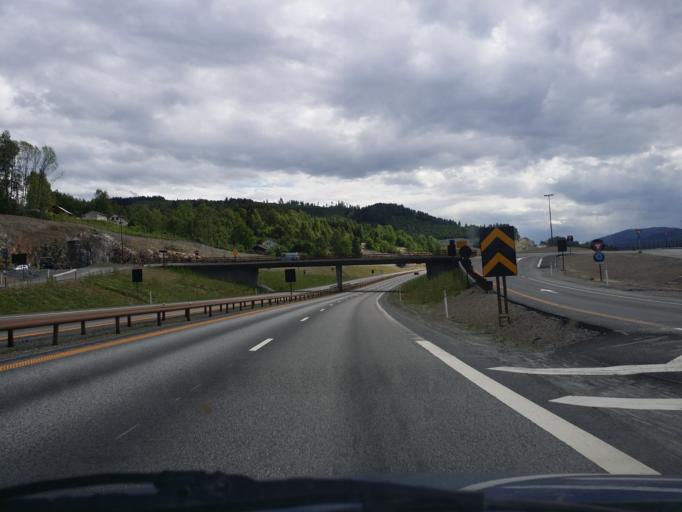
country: NO
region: Akershus
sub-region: Eidsvoll
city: Eidsvoll
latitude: 60.5159
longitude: 11.2438
